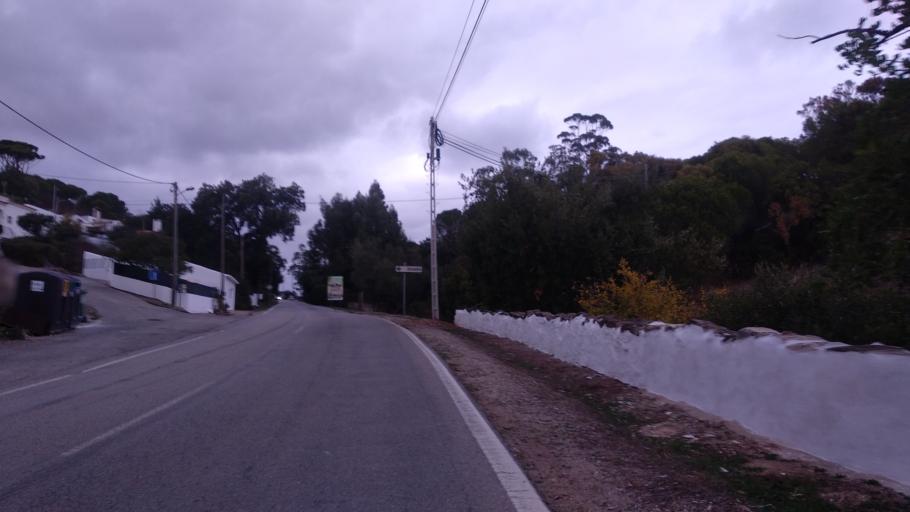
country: PT
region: Faro
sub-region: Sao Bras de Alportel
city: Sao Bras de Alportel
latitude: 37.1772
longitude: -7.9096
